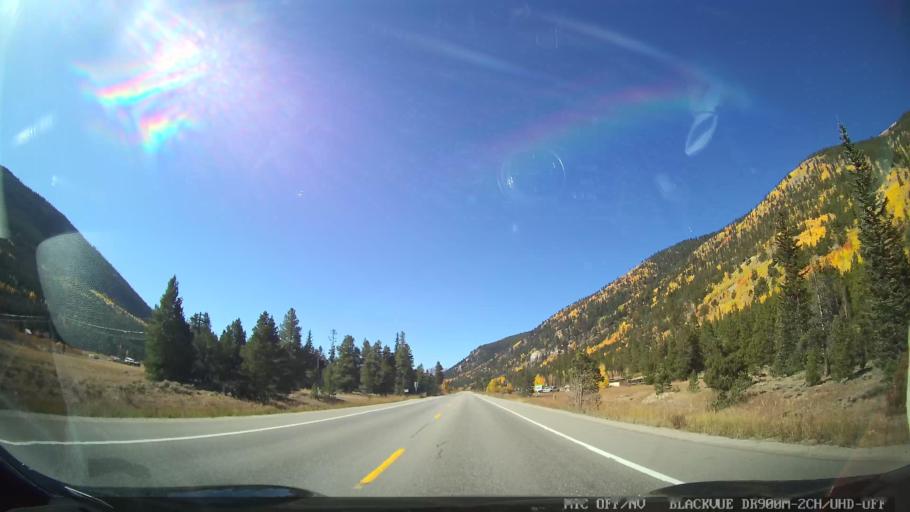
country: US
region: Colorado
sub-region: Lake County
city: Leadville North
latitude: 39.3018
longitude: -106.2636
